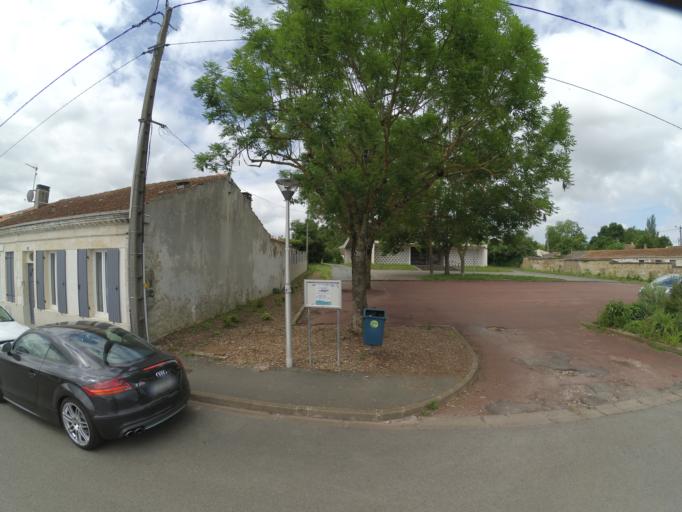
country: FR
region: Poitou-Charentes
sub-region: Departement de la Charente-Maritime
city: Rochefort
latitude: 45.9495
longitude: -0.9685
